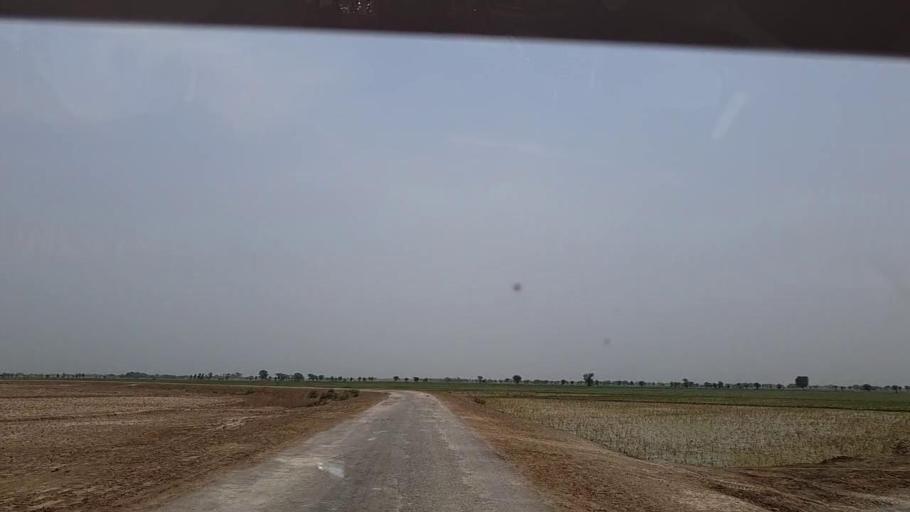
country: PK
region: Sindh
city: Khairpur Nathan Shah
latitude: 27.0188
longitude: 67.6448
